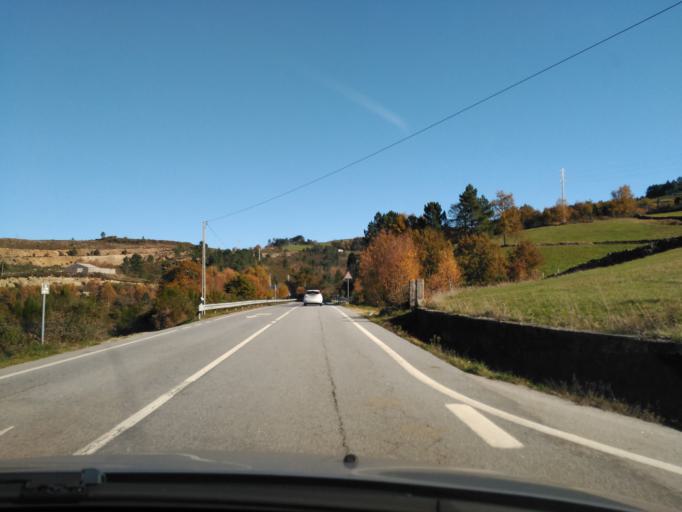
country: PT
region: Vila Real
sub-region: Montalegre
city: Montalegre
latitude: 41.7007
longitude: -7.9284
